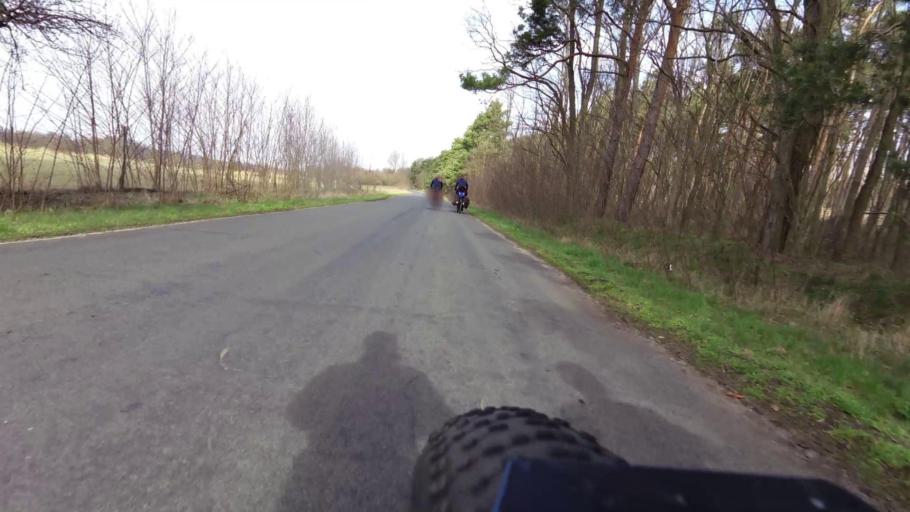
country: DE
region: Brandenburg
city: Brieskow-Finkenheerd
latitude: 52.2898
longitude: 14.6109
